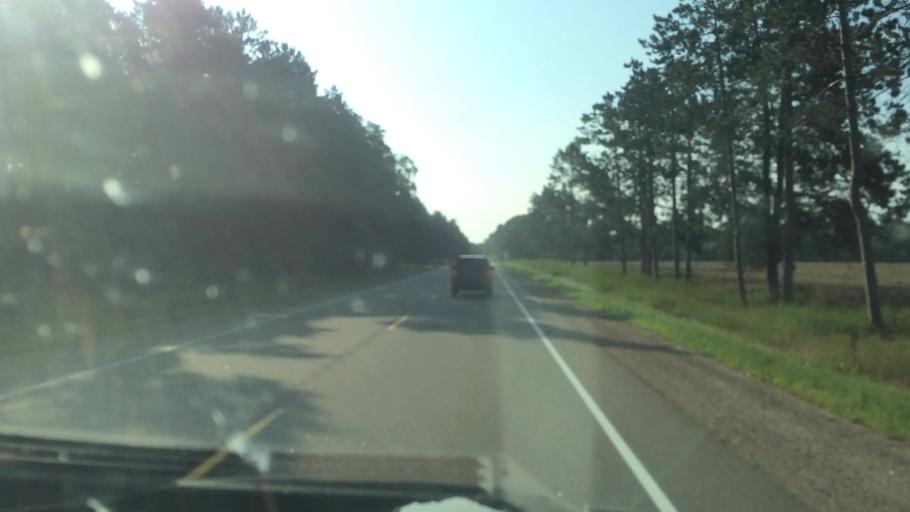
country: US
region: Wisconsin
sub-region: Langlade County
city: Antigo
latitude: 45.1444
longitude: -89.2434
